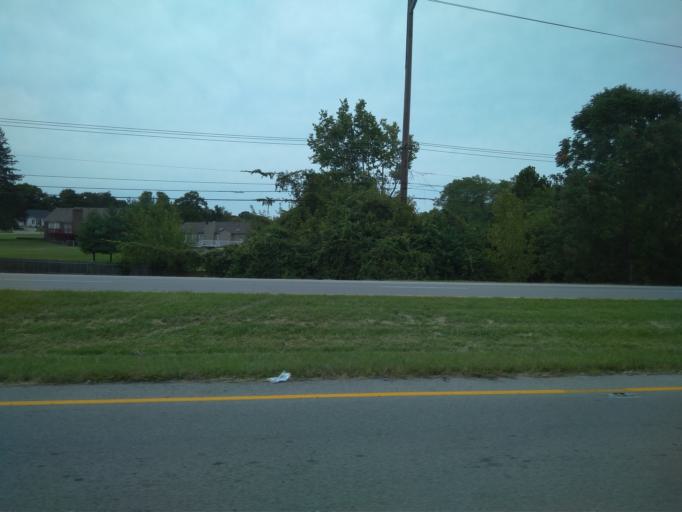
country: US
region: Kentucky
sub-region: Jefferson County
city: Hurstbourne
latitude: 38.2323
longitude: -85.5770
